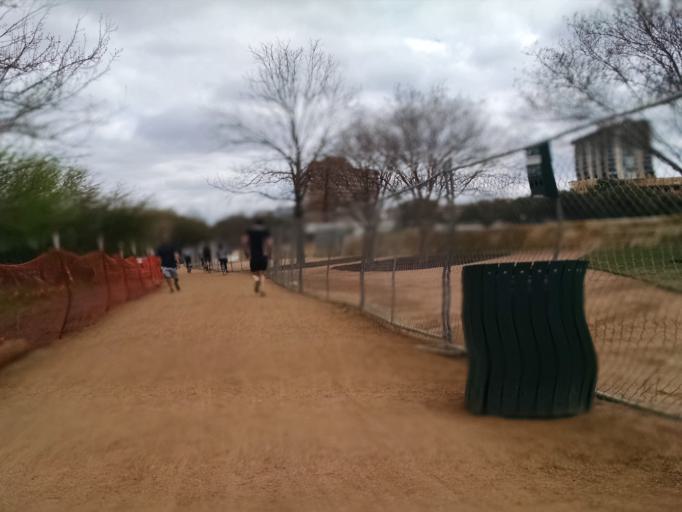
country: US
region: Texas
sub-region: Travis County
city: Austin
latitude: 30.2631
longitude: -97.7506
